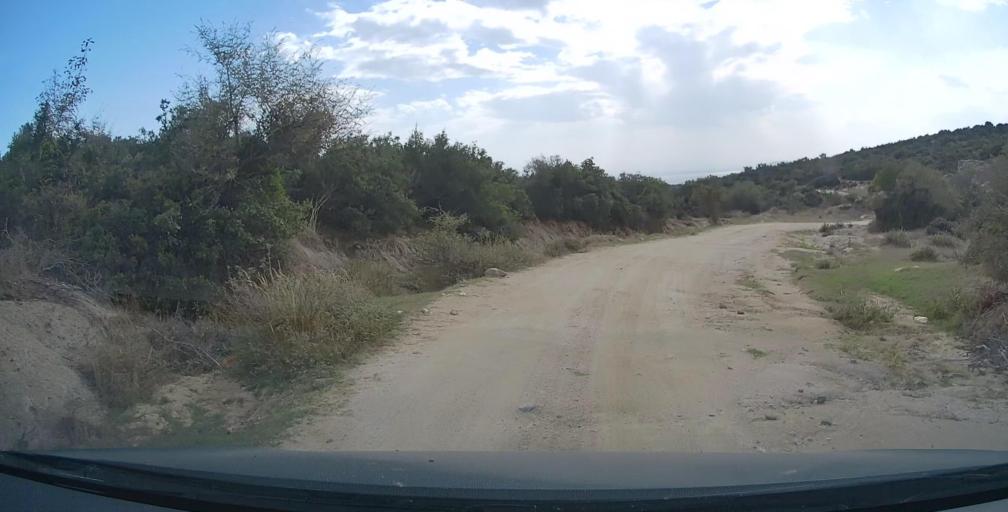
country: GR
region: Central Macedonia
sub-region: Nomos Chalkidikis
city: Sykia
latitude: 40.0124
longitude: 23.9306
